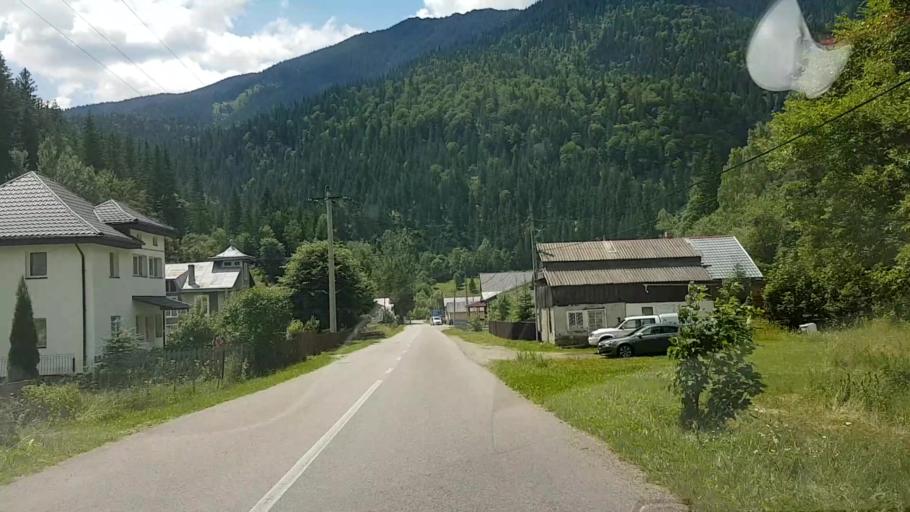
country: RO
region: Suceava
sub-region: Comuna Crucea
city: Crucea
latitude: 47.3986
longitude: 25.5661
